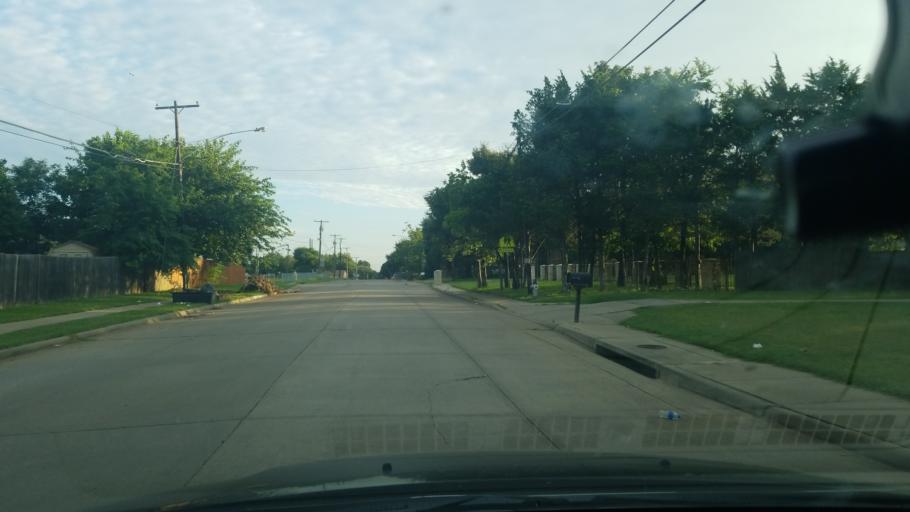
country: US
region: Texas
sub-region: Dallas County
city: Balch Springs
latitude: 32.7386
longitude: -96.6398
